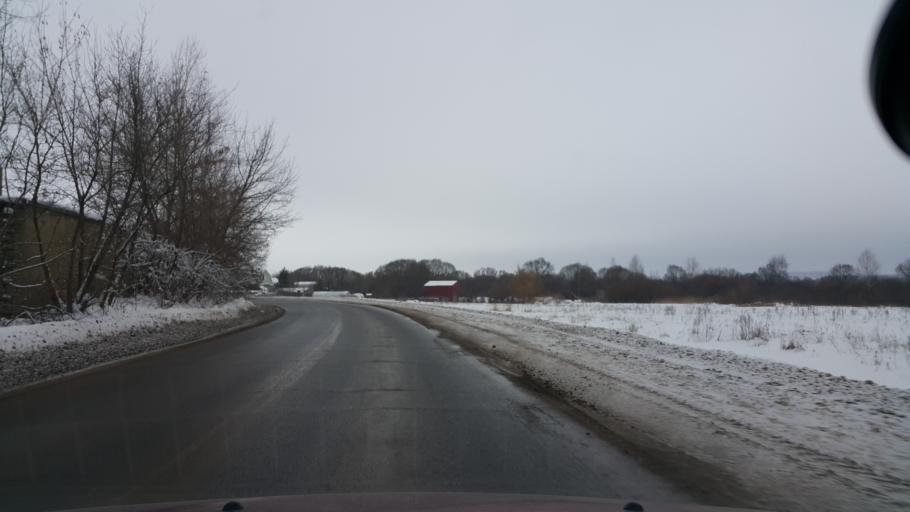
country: RU
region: Tambov
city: Pokrovo-Prigorodnoye
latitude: 52.6603
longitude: 41.4361
